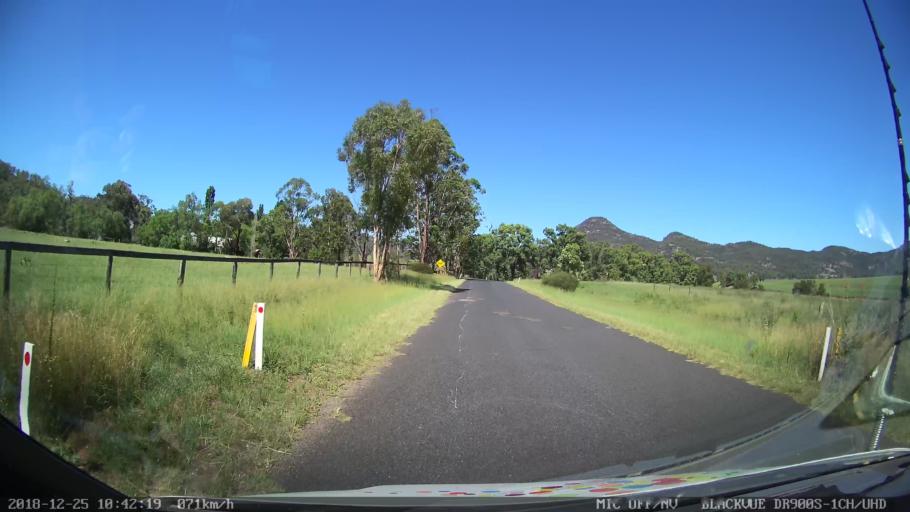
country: AU
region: New South Wales
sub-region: Upper Hunter Shire
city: Merriwa
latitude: -32.4154
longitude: 150.3247
